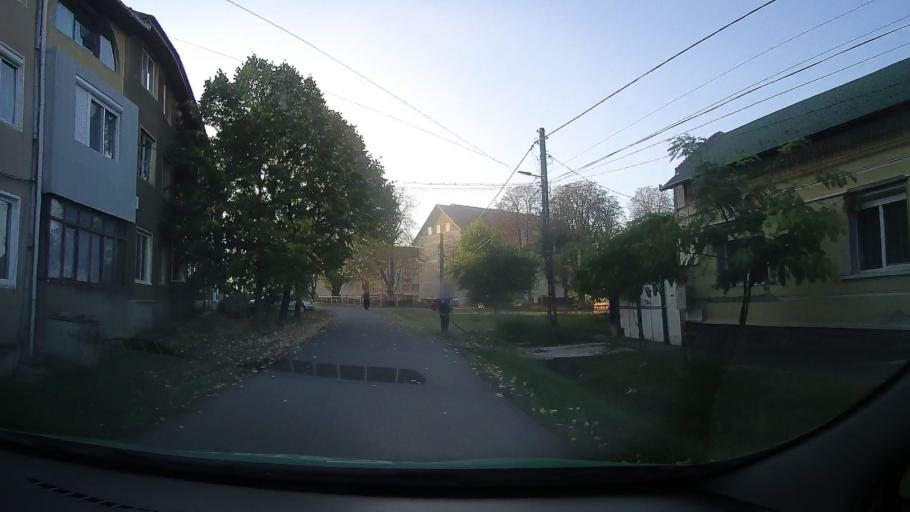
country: RO
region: Bihor
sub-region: Comuna Salard
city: Salard
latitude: 47.2251
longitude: 22.0293
